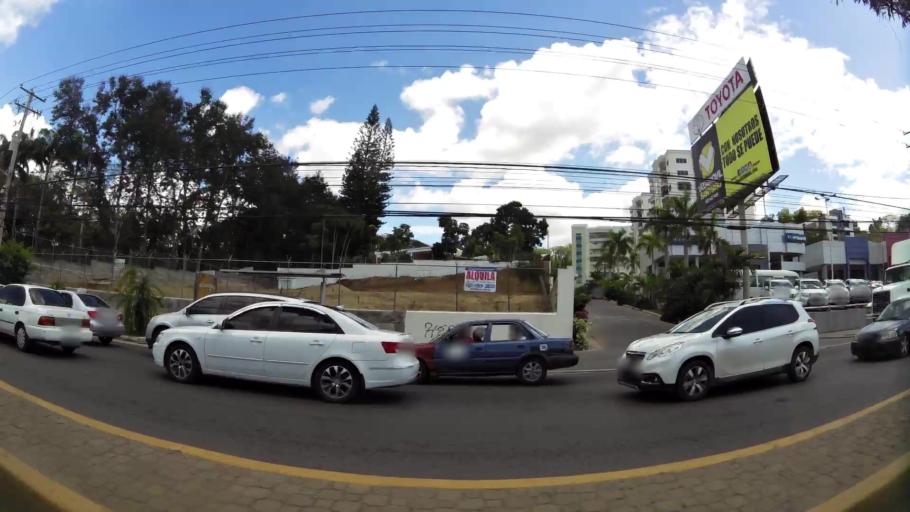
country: DO
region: Santiago
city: Santiago de los Caballeros
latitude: 19.4667
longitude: -70.6868
